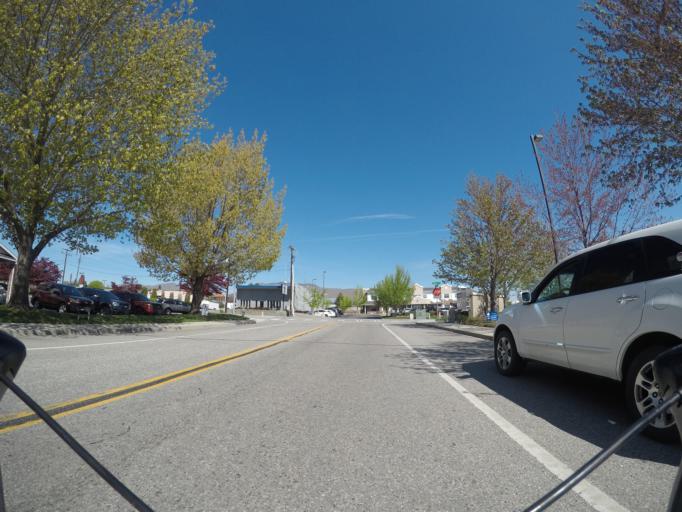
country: US
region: Washington
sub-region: Chelan County
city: Sunnyslope
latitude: 47.4656
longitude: -120.3340
